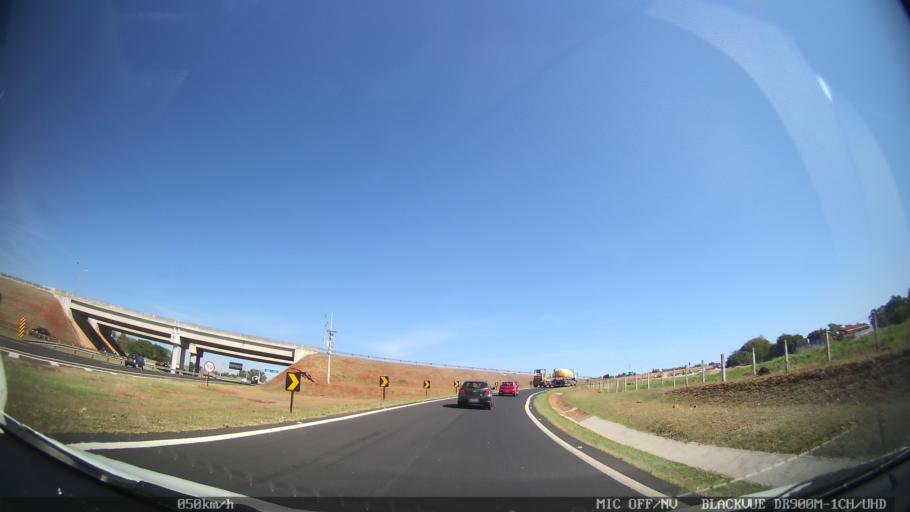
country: BR
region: Sao Paulo
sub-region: Ribeirao Preto
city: Ribeirao Preto
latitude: -21.2219
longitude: -47.7765
